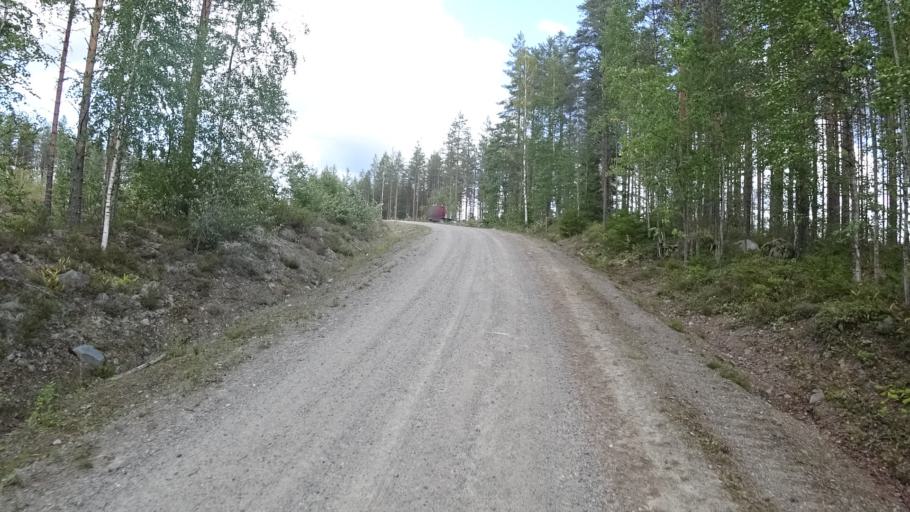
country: FI
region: North Karelia
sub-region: Joensuu
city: Ilomantsi
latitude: 62.6210
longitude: 31.2463
